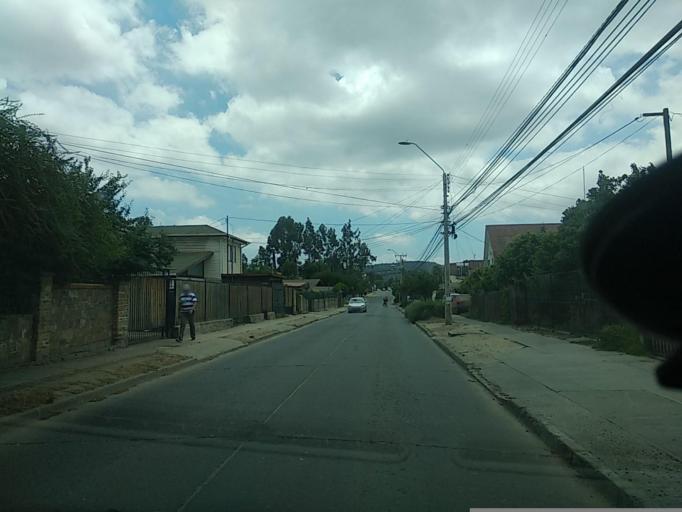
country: CL
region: Valparaiso
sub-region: Provincia de Marga Marga
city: Villa Alemana
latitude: -33.0417
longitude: -71.4054
